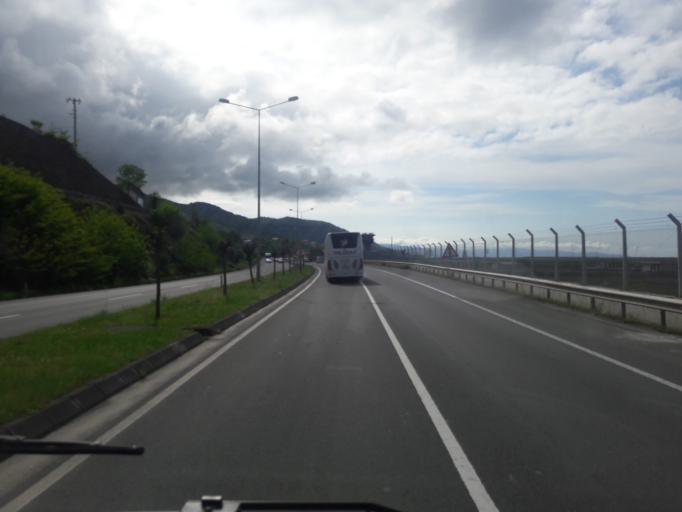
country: TR
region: Ordu
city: Gulyali
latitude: 40.9629
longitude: 38.0898
